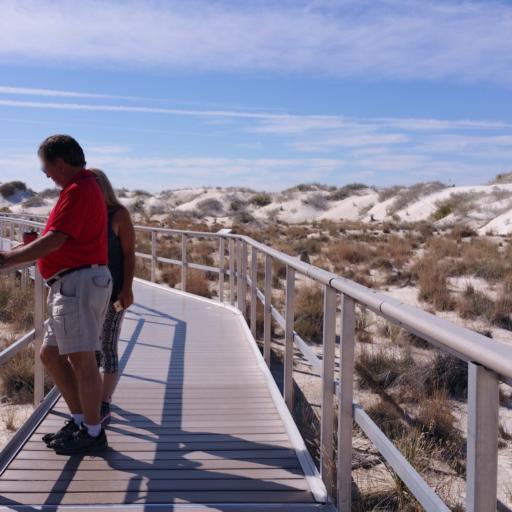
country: US
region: New Mexico
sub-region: Otero County
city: Holloman Air Force Base
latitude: 32.7950
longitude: -106.2390
